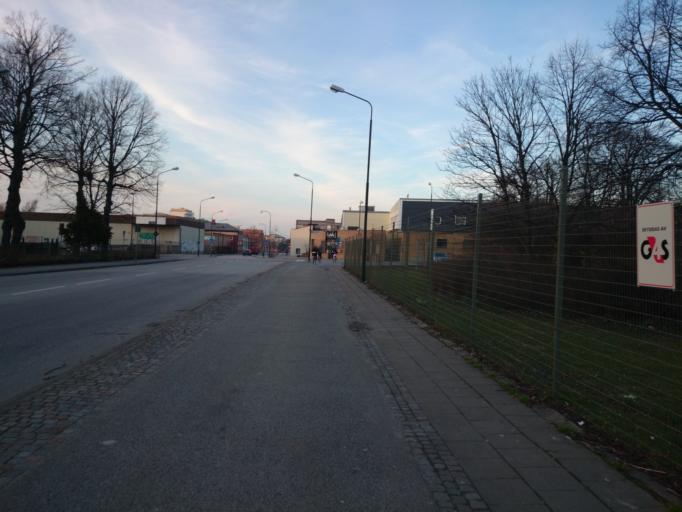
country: SE
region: Skane
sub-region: Malmo
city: Malmoe
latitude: 55.5960
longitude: 13.0290
